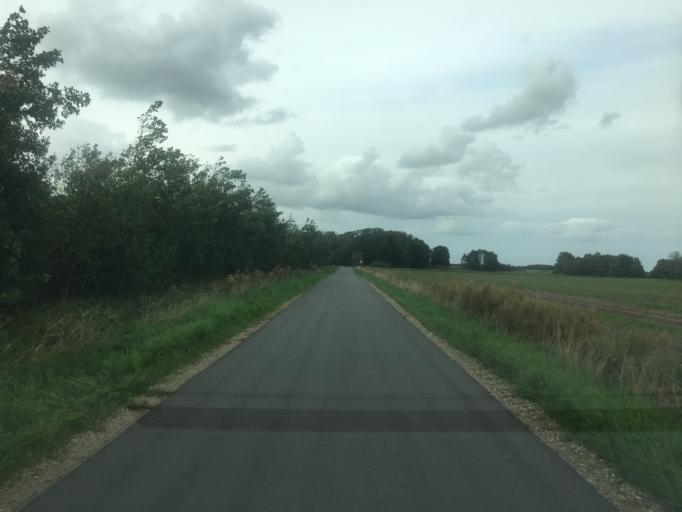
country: DE
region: Schleswig-Holstein
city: Aventoft
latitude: 54.9580
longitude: 8.8023
